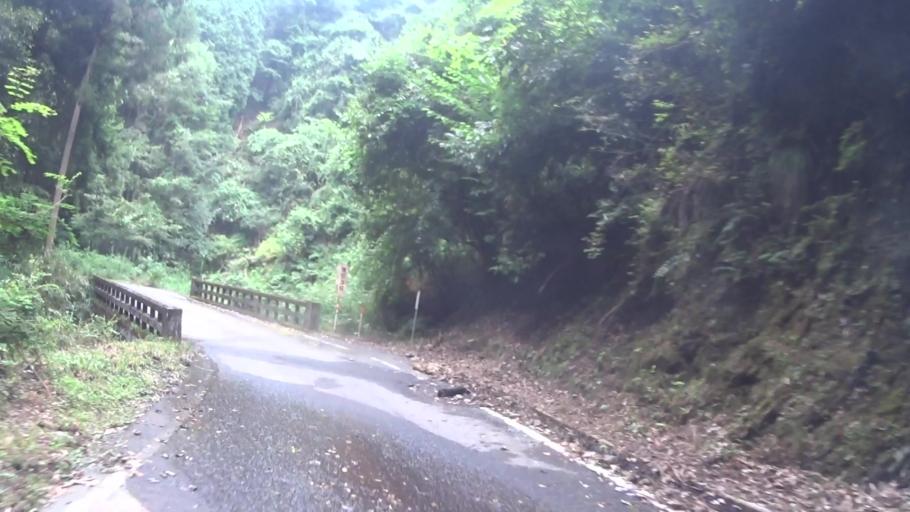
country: JP
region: Kyoto
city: Kameoka
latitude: 35.1515
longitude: 135.5725
